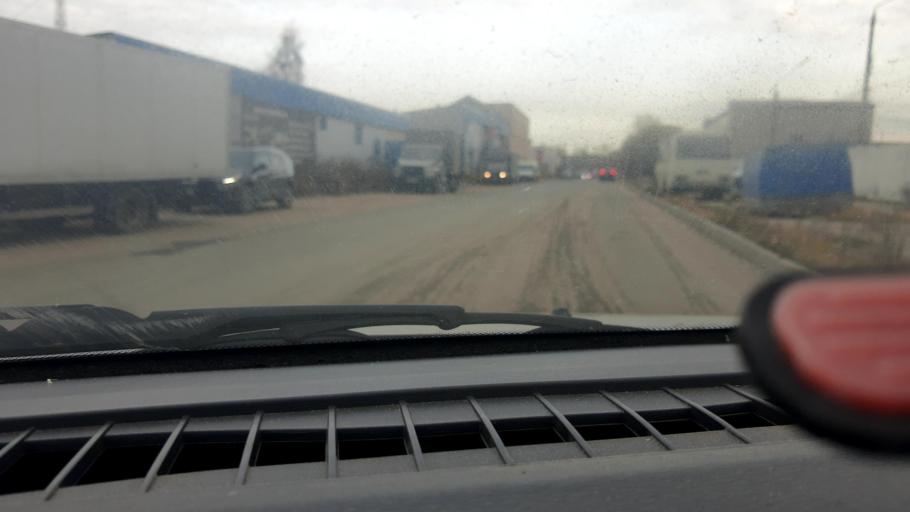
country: RU
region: Nizjnij Novgorod
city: Nizhniy Novgorod
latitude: 56.2923
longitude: 43.8759
